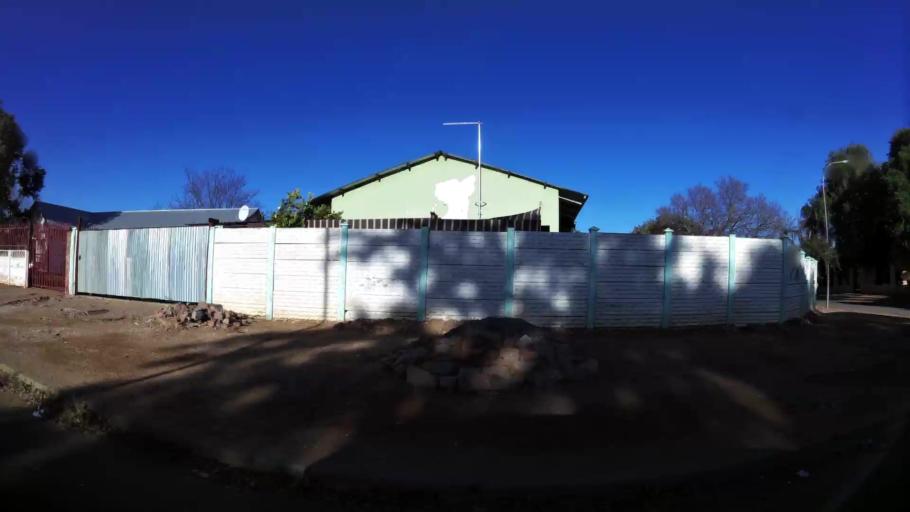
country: ZA
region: Northern Cape
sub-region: Frances Baard District Municipality
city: Kimberley
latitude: -28.7391
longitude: 24.7389
